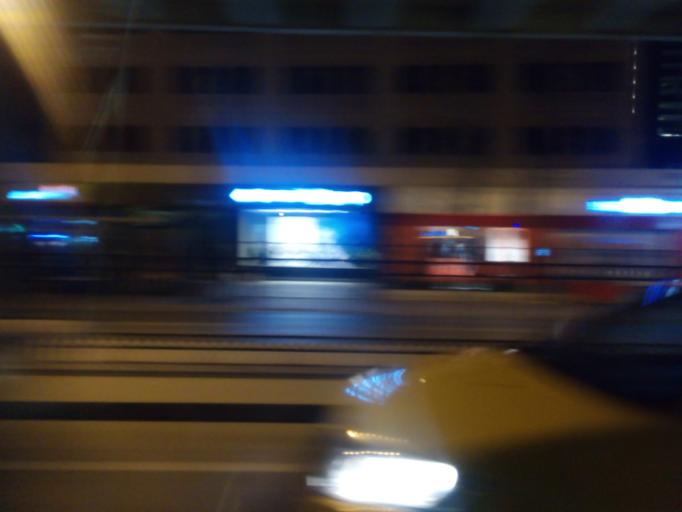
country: TR
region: Istanbul
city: Sisli
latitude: 41.0661
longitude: 29.0008
